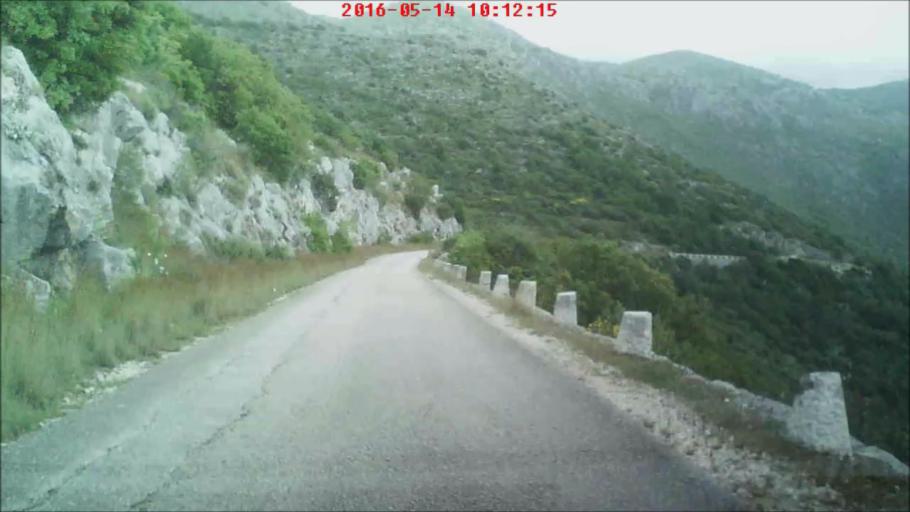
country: HR
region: Dubrovacko-Neretvanska
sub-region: Grad Dubrovnik
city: Mokosica
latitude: 42.7352
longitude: 17.9474
